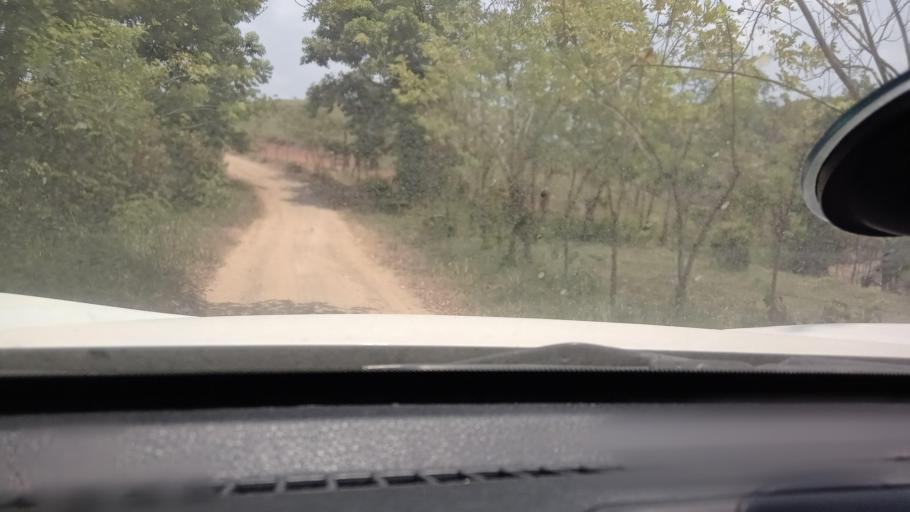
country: MX
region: Tabasco
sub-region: Huimanguillo
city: Francisco Rueda
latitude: 17.4923
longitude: -93.9160
